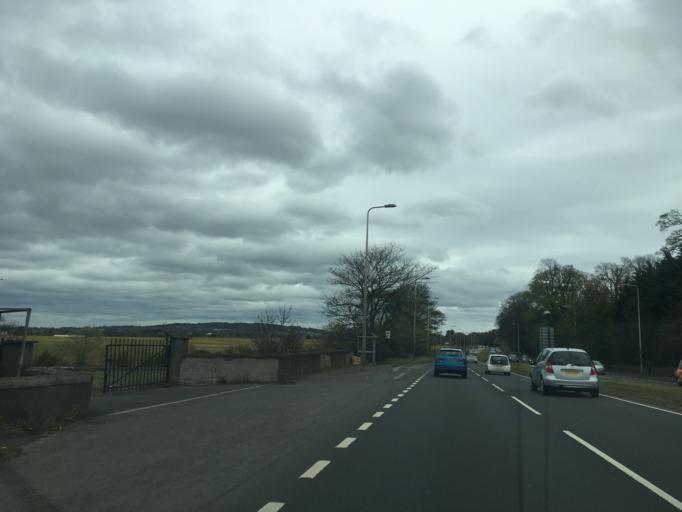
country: GB
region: Scotland
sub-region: Edinburgh
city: Ratho
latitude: 55.9369
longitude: -3.3519
